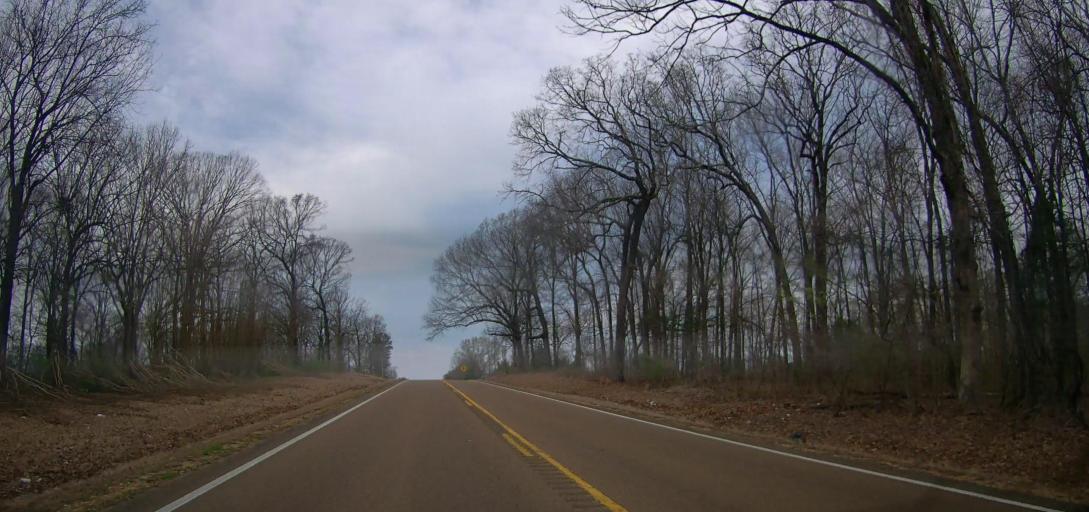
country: US
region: Mississippi
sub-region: Marshall County
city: Byhalia
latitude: 34.8352
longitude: -89.5858
